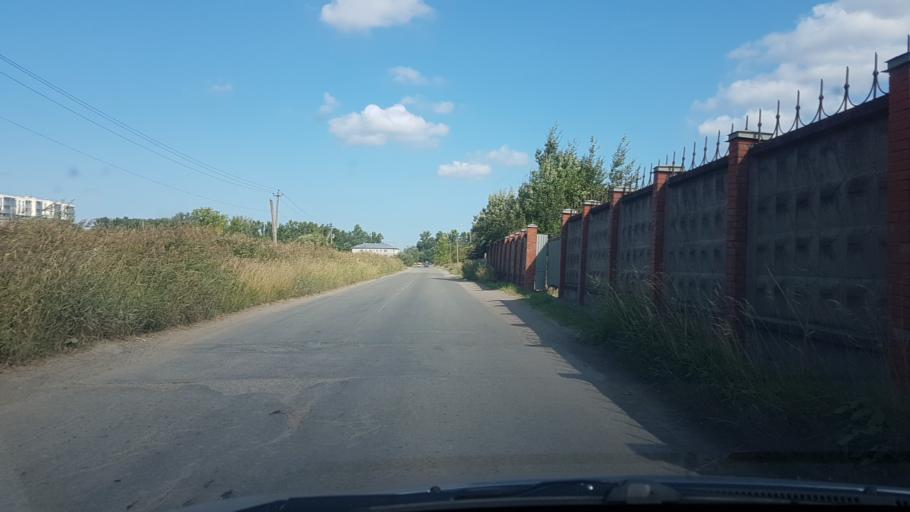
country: RU
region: St.-Petersburg
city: Sosnovaya Polyana
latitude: 59.8430
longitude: 30.1195
